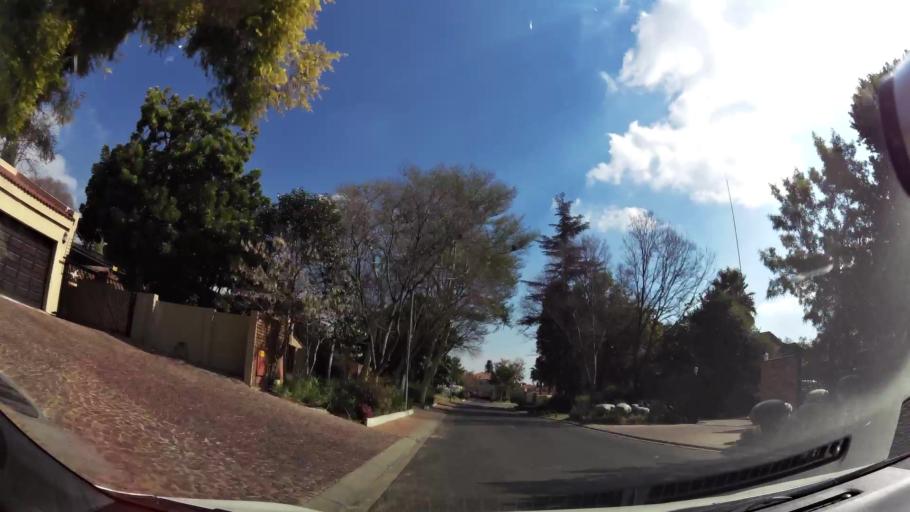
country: ZA
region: Gauteng
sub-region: City of Johannesburg Metropolitan Municipality
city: Midrand
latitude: -26.0255
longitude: 28.0732
